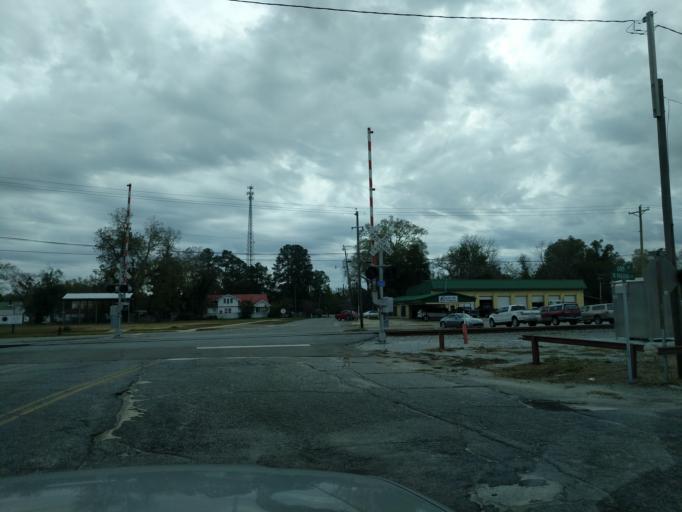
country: US
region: South Carolina
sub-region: Lexington County
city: Batesburg
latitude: 33.9066
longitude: -81.5482
